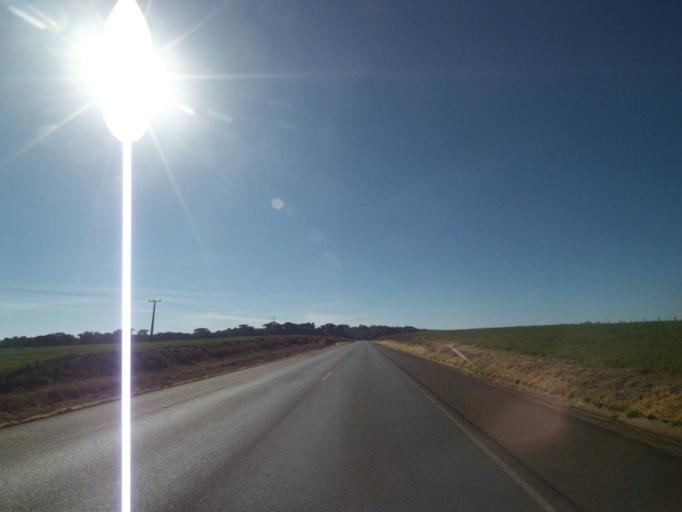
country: BR
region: Parana
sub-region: Tibagi
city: Tibagi
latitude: -24.4287
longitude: -50.4036
